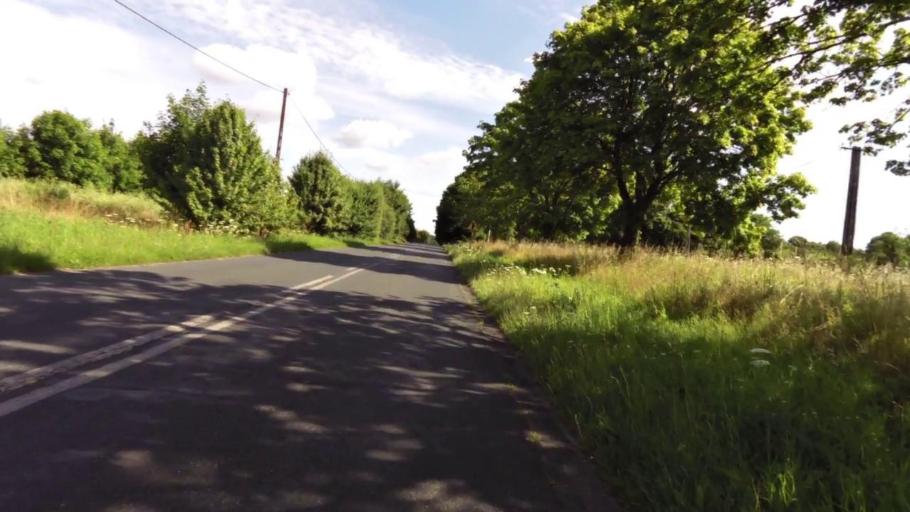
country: PL
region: West Pomeranian Voivodeship
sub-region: Powiat stargardzki
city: Dobrzany
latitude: 53.3717
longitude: 15.4331
